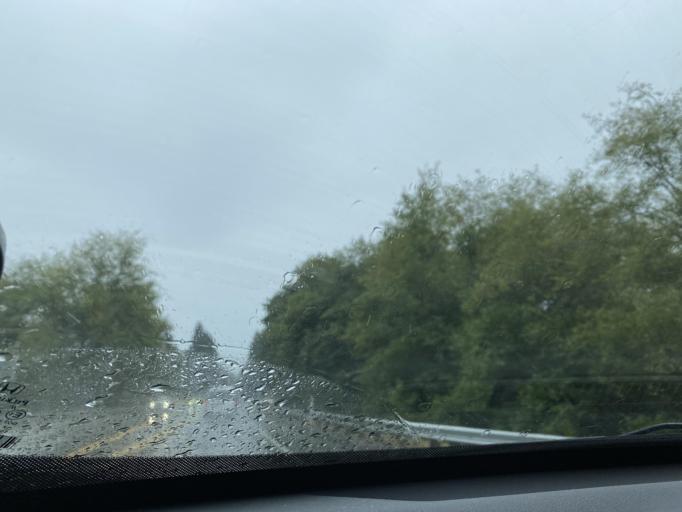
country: US
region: Washington
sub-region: Kitsap County
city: Bainbridge Island
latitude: 47.6734
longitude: -122.5331
